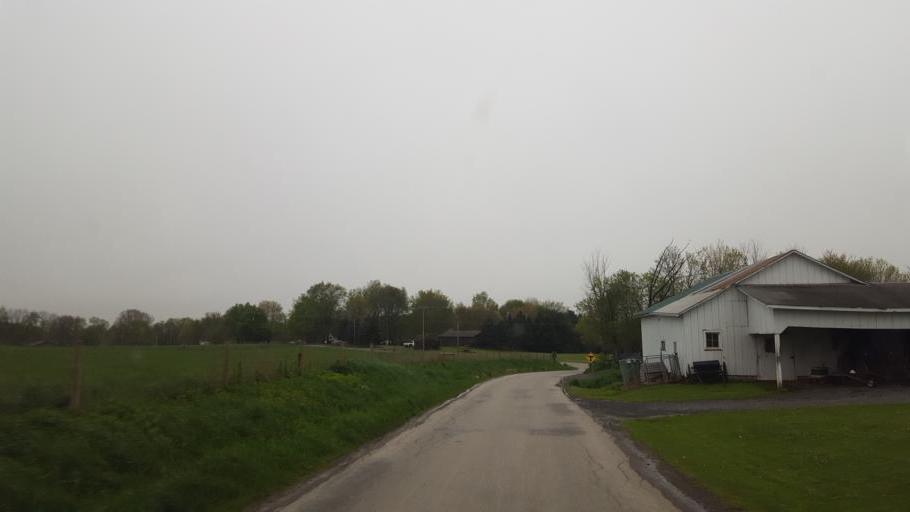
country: US
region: Pennsylvania
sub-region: Mercer County
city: Stoneboro
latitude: 41.2952
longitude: -80.1732
